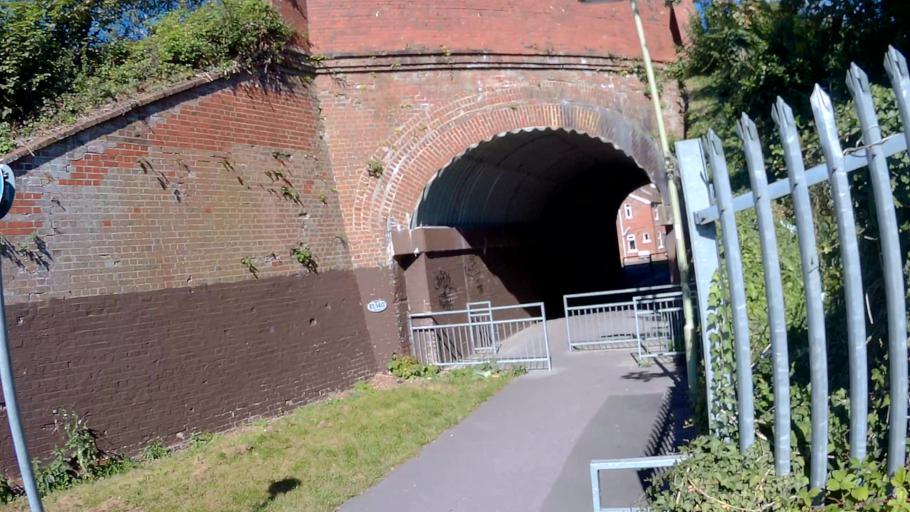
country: GB
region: England
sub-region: Hampshire
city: Basingstoke
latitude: 51.2622
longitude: -1.1348
